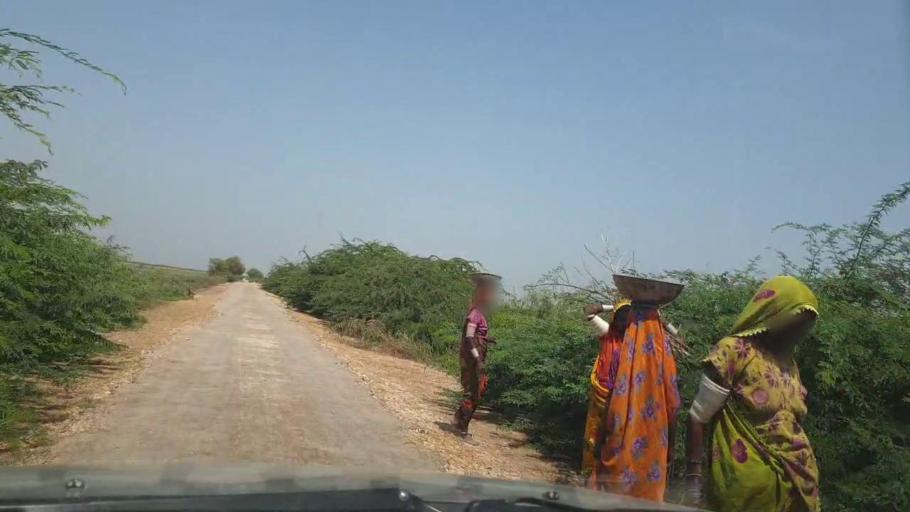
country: PK
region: Sindh
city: Tando Ghulam Ali
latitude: 25.1064
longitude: 68.8021
